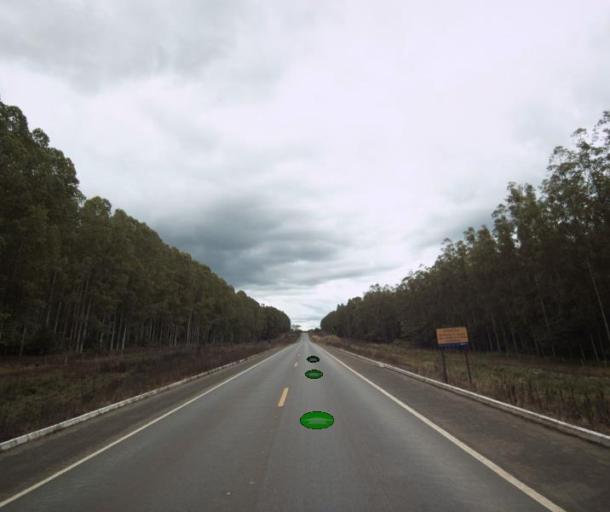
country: BR
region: Goias
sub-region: Niquelandia
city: Niquelandia
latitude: -14.5695
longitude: -48.5628
